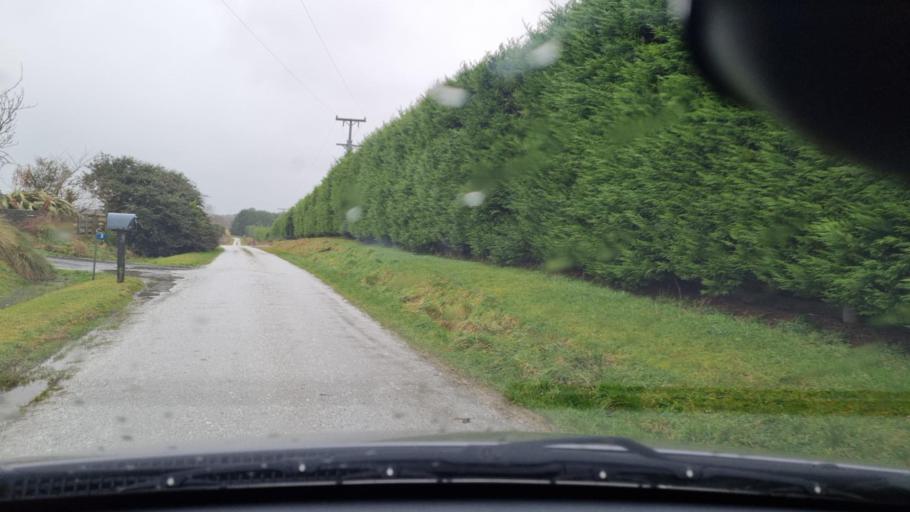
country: NZ
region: Southland
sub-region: Invercargill City
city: Invercargill
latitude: -46.3920
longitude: 168.4056
